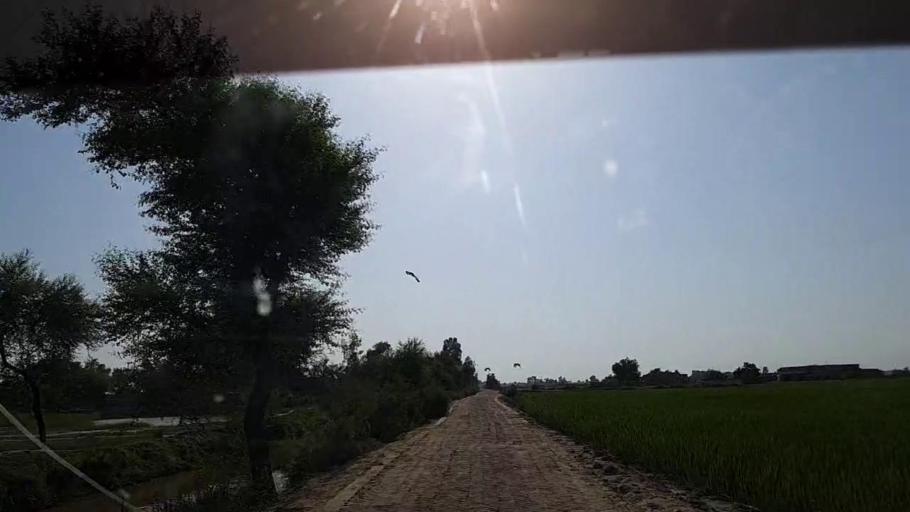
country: PK
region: Sindh
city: Tangwani
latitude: 28.2142
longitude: 68.9641
